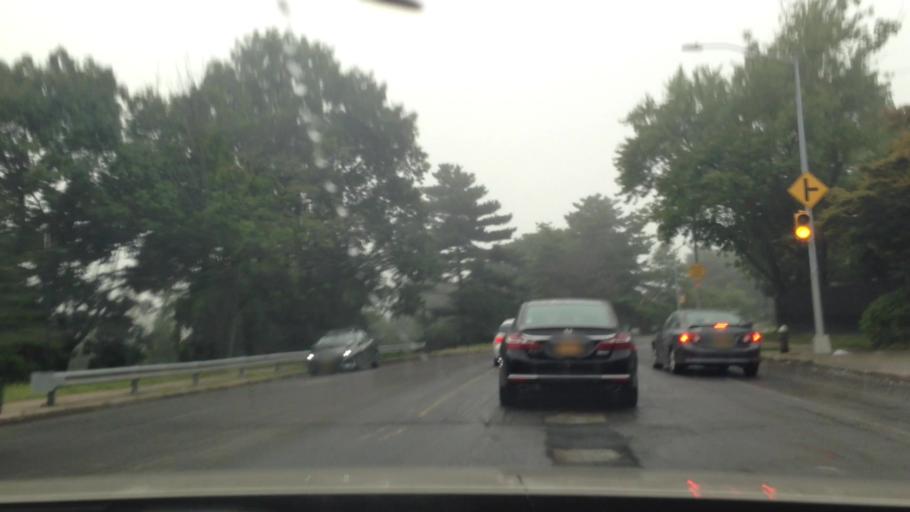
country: US
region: New York
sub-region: Nassau County
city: Lake Success
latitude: 40.7530
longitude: -73.7416
